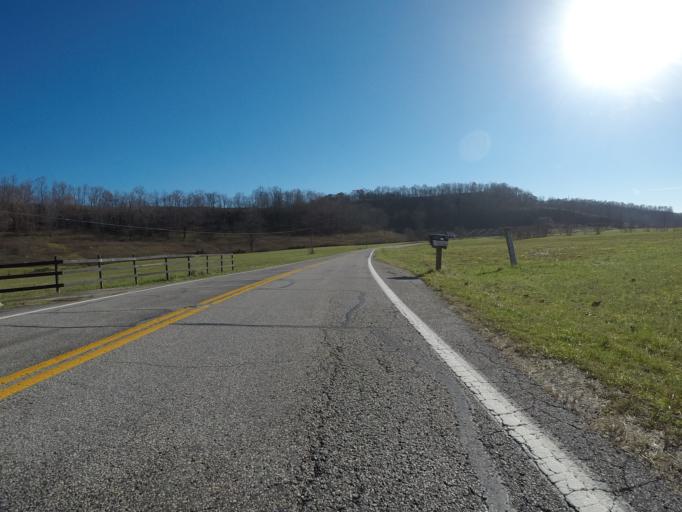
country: US
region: West Virginia
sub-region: Cabell County
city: Huntington
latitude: 38.4851
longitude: -82.4495
